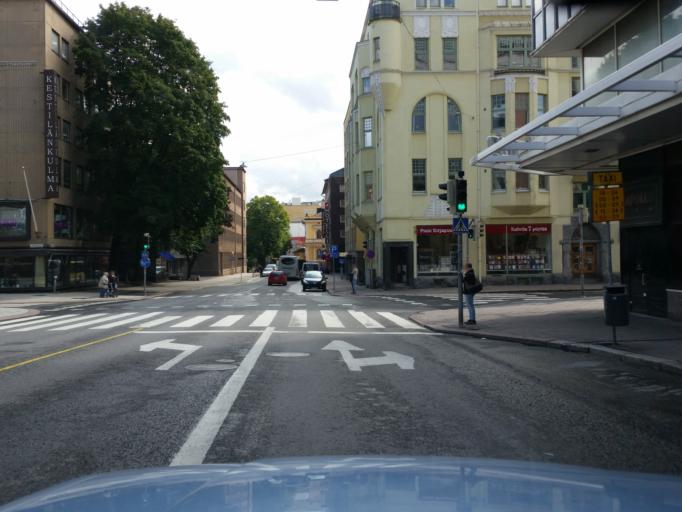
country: FI
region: Varsinais-Suomi
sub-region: Turku
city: Turku
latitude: 60.4502
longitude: 22.2596
